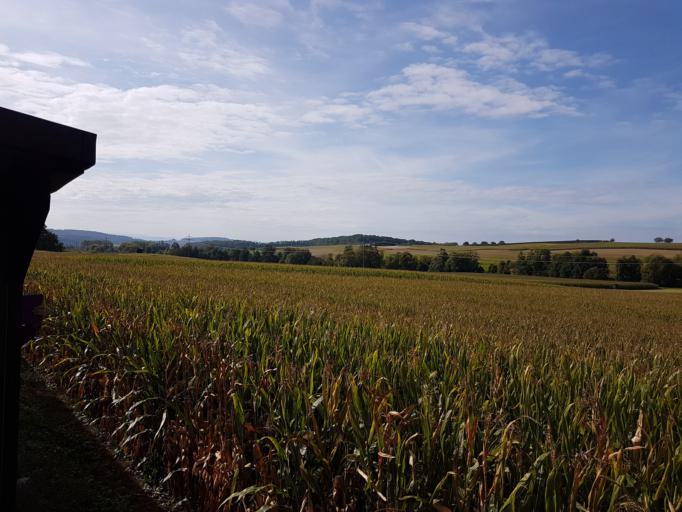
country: DE
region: Baden-Wuerttemberg
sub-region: Freiburg Region
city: Wittlingen
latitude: 47.6823
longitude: 7.6445
